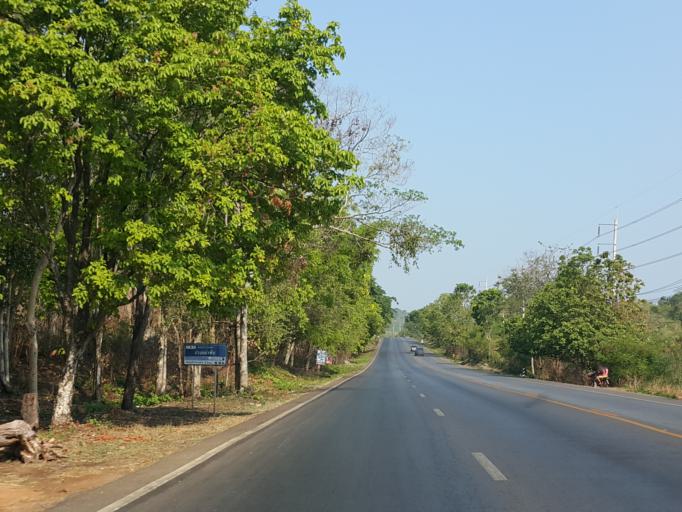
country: TH
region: Kanchanaburi
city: Sai Yok
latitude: 14.1086
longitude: 99.2141
